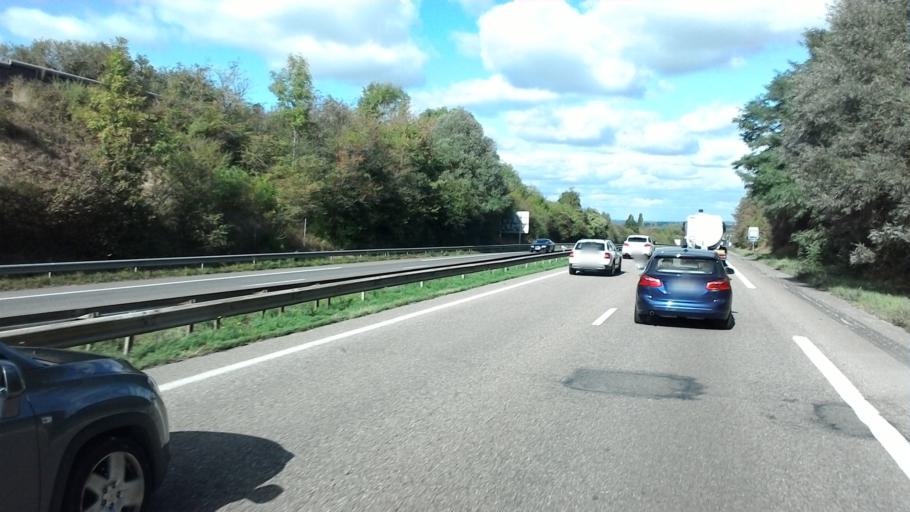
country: FR
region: Lorraine
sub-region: Departement de Meurthe-et-Moselle
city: Dommartin-les-Toul
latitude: 48.6655
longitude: 5.9142
